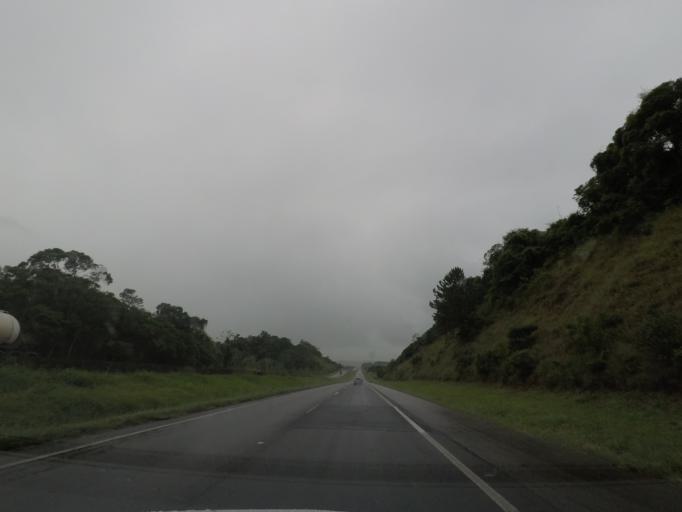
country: BR
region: Sao Paulo
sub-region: Registro
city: Registro
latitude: -24.4405
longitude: -47.7973
